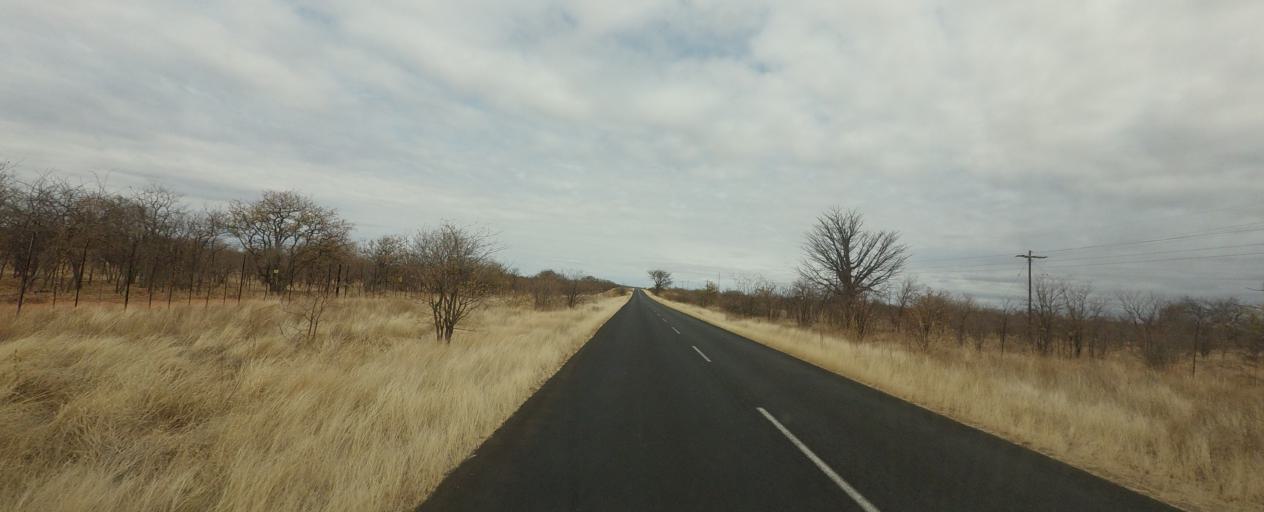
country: ZW
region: Matabeleland South
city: Beitbridge
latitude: -22.4310
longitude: 29.4556
